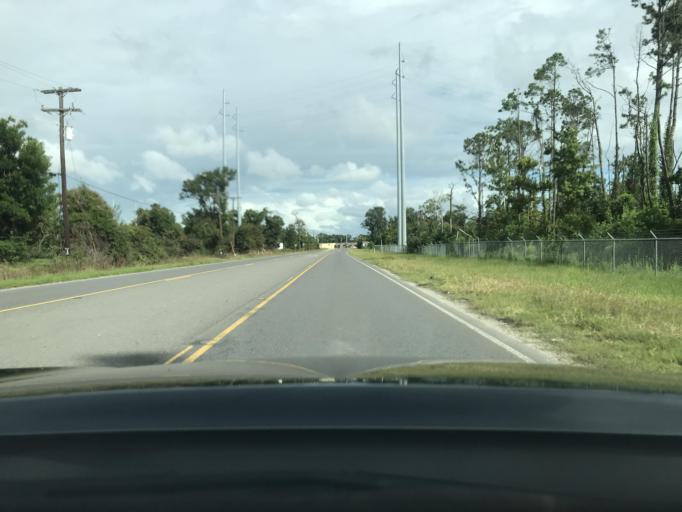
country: US
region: Louisiana
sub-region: Calcasieu Parish
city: Westlake
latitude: 30.2508
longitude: -93.2707
